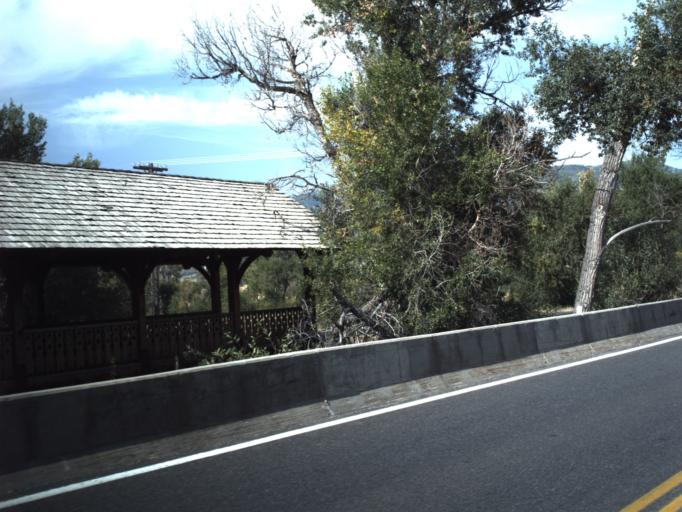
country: US
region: Utah
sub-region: Wasatch County
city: Midway
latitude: 40.5074
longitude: -111.4497
